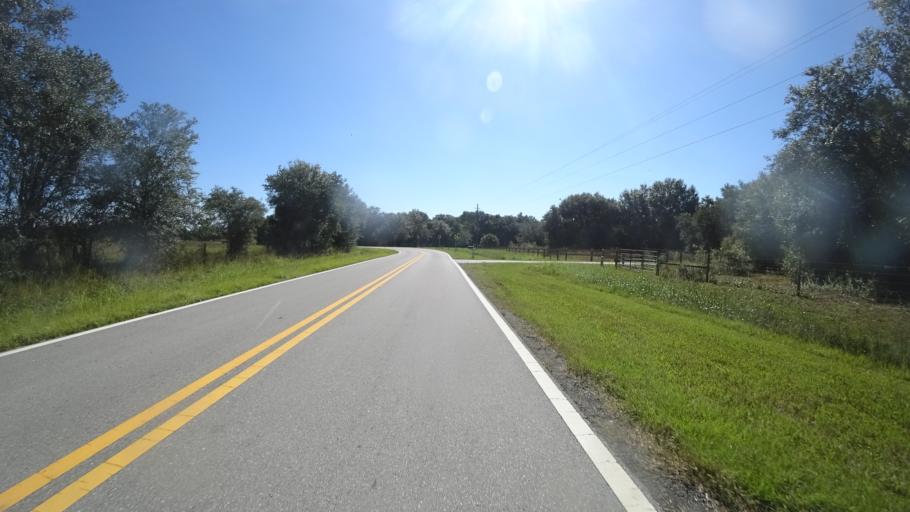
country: US
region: Florida
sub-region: Sarasota County
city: Lake Sarasota
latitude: 27.2894
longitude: -82.2335
